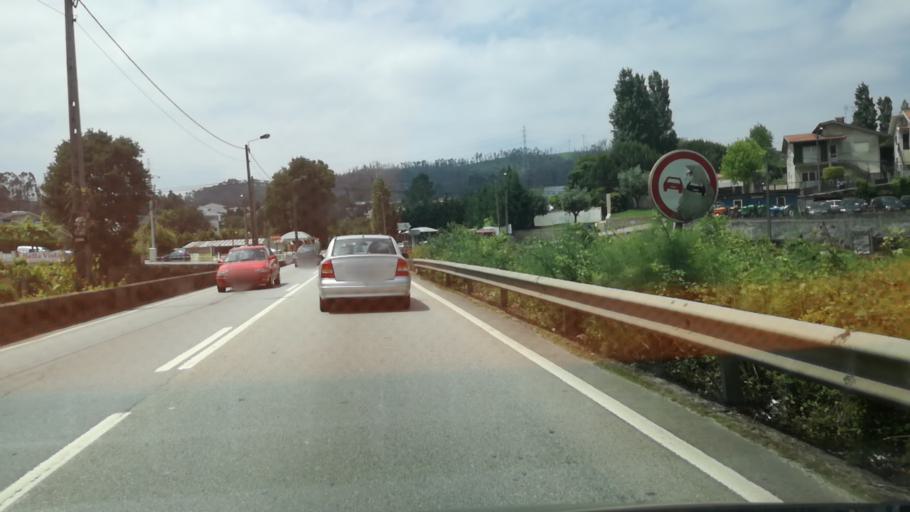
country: PT
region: Porto
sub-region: Trofa
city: Bougado
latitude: 41.3171
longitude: -8.5762
